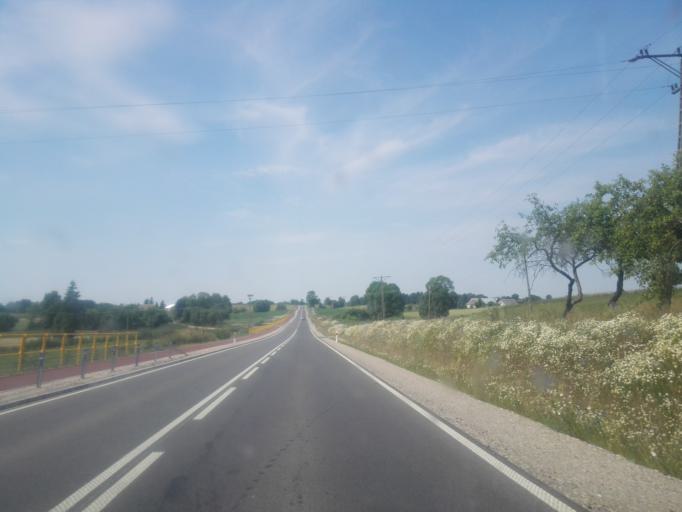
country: PL
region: Podlasie
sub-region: Powiat sejnenski
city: Sejny
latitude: 54.1094
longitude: 23.3013
